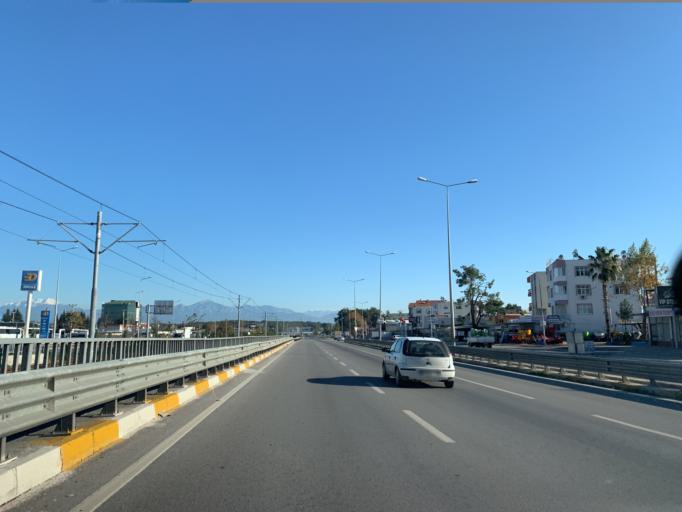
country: TR
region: Antalya
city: Aksu
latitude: 36.9383
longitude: 30.8191
